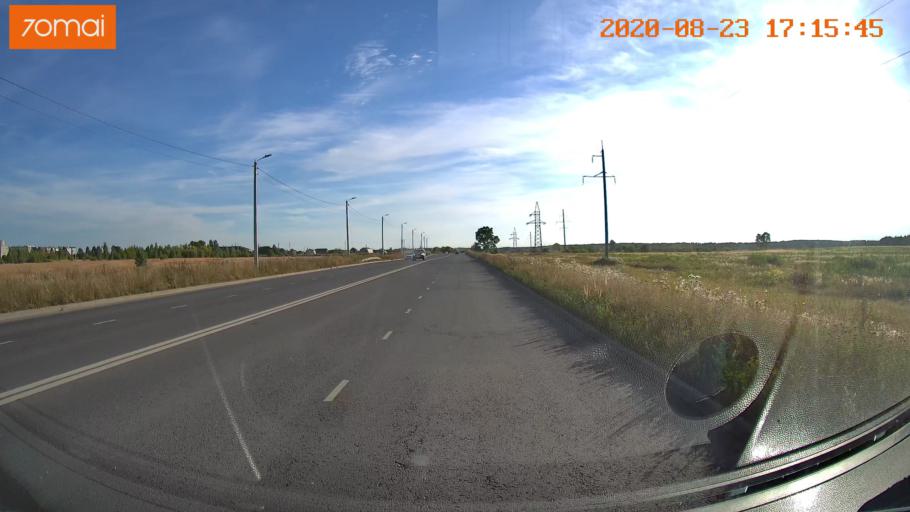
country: RU
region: Ivanovo
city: Novo-Talitsy
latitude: 57.0432
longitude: 40.9081
